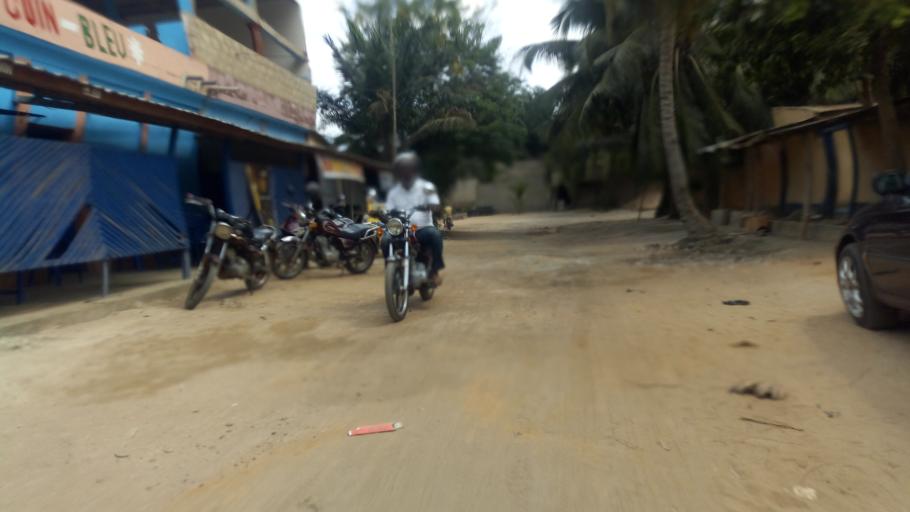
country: TG
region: Maritime
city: Tsevie
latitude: 6.3204
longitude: 1.2253
